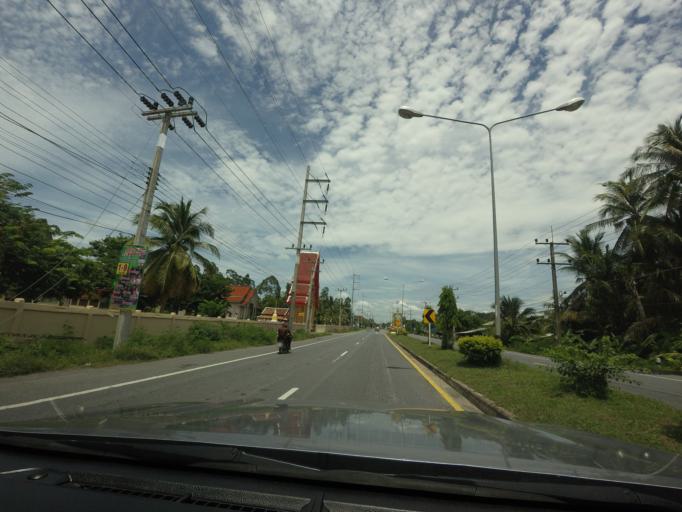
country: TH
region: Songkhla
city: Sathing Phra
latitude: 7.5646
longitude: 100.4115
